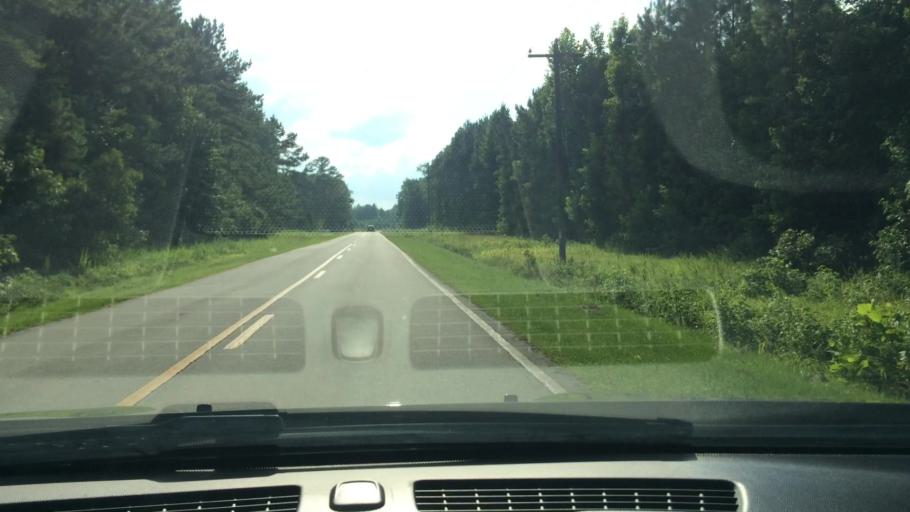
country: US
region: North Carolina
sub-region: Beaufort County
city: River Road
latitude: 35.4360
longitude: -76.9891
